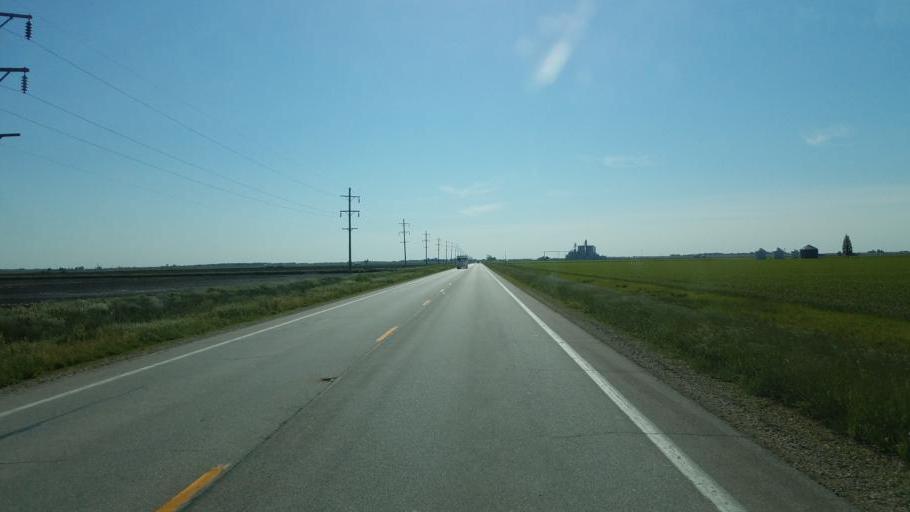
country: US
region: Illinois
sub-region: McDonough County
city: Bushnell
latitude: 40.4544
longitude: -90.5321
